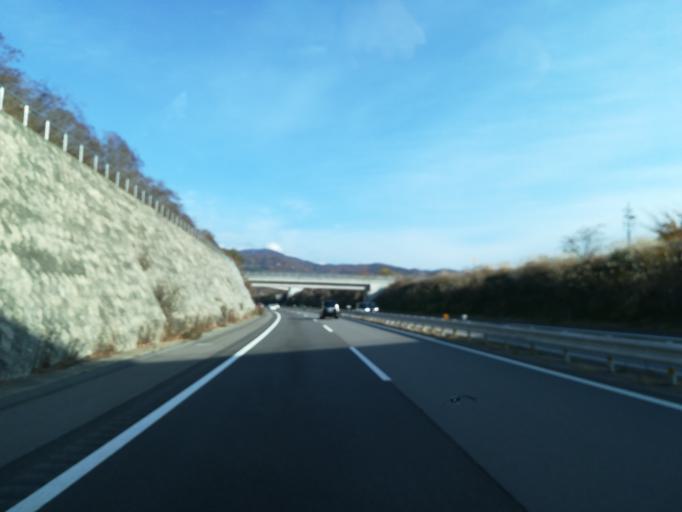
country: JP
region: Nagano
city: Ueda
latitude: 36.4095
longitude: 138.2922
